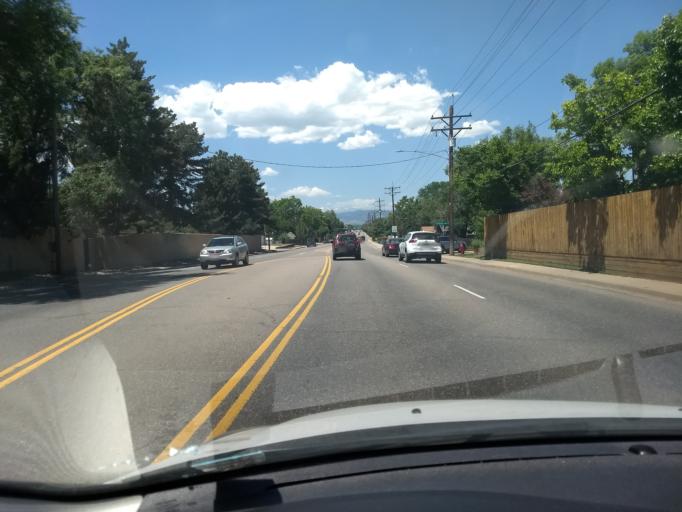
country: US
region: Colorado
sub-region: Arapahoe County
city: Englewood
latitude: 39.6241
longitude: -104.9792
